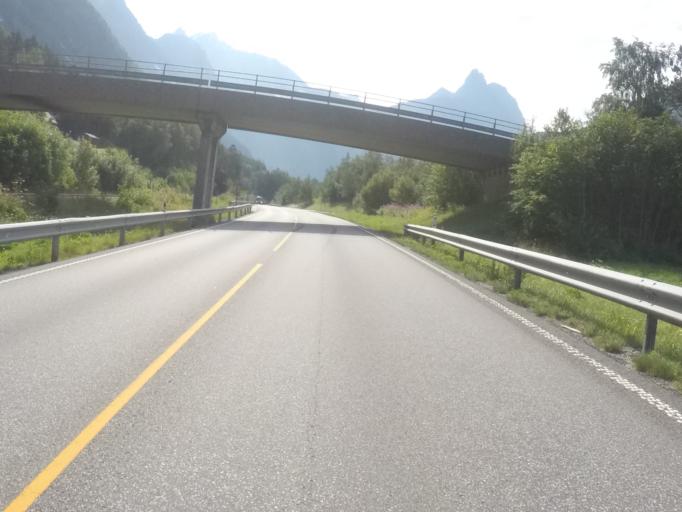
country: NO
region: More og Romsdal
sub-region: Rauma
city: Andalsnes
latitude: 62.5403
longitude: 7.7227
